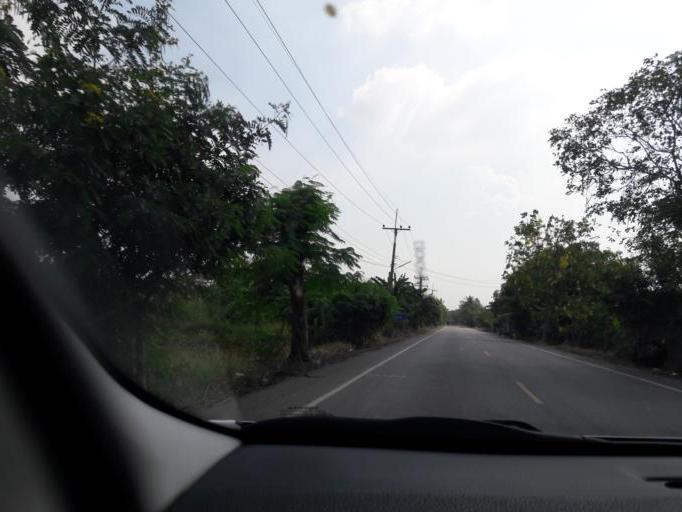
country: TH
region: Ang Thong
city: Ang Thong
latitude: 14.5767
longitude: 100.4281
